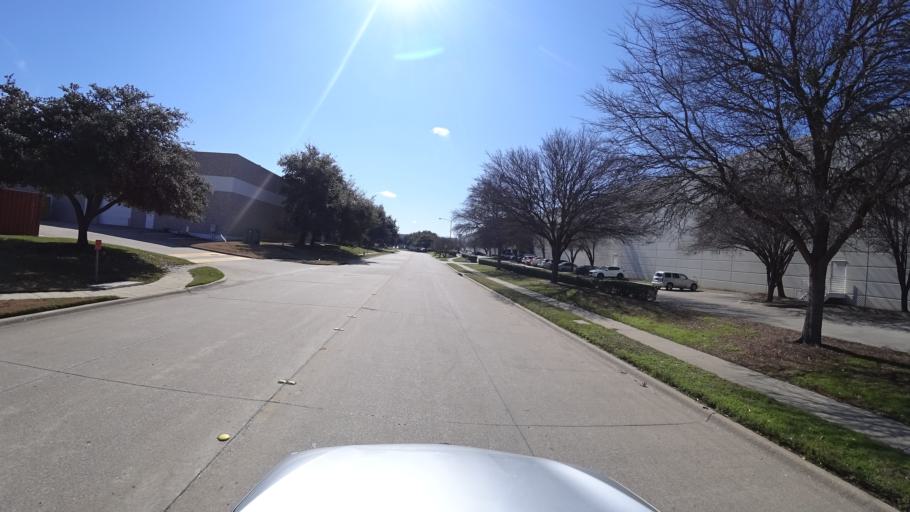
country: US
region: Texas
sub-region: Denton County
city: Lewisville
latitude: 33.0243
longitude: -96.9789
